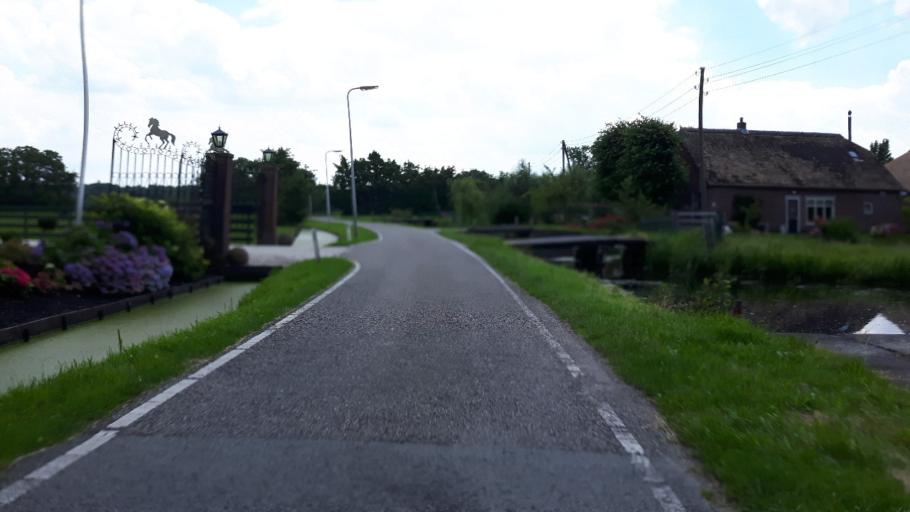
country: NL
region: South Holland
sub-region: Bodegraven-Reeuwijk
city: Bodegraven
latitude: 52.0745
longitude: 4.7341
